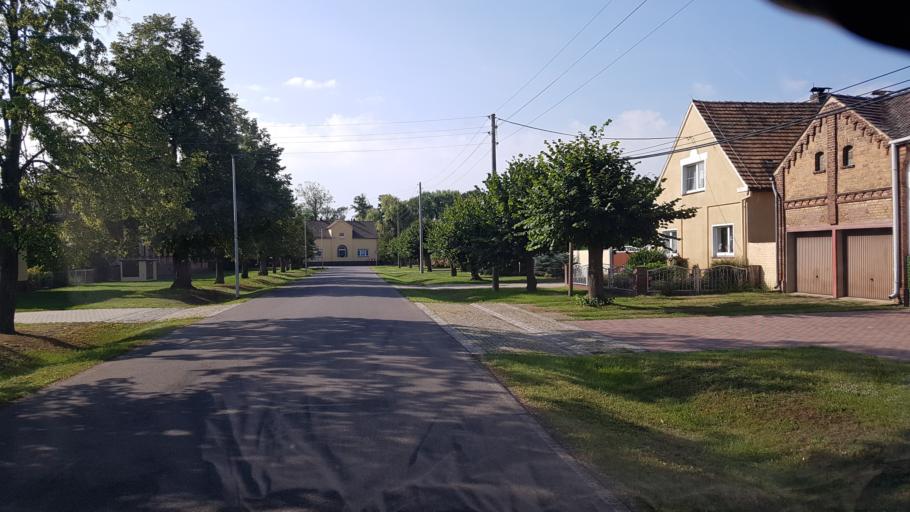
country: DE
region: Brandenburg
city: Luebben
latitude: 51.8676
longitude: 13.8570
